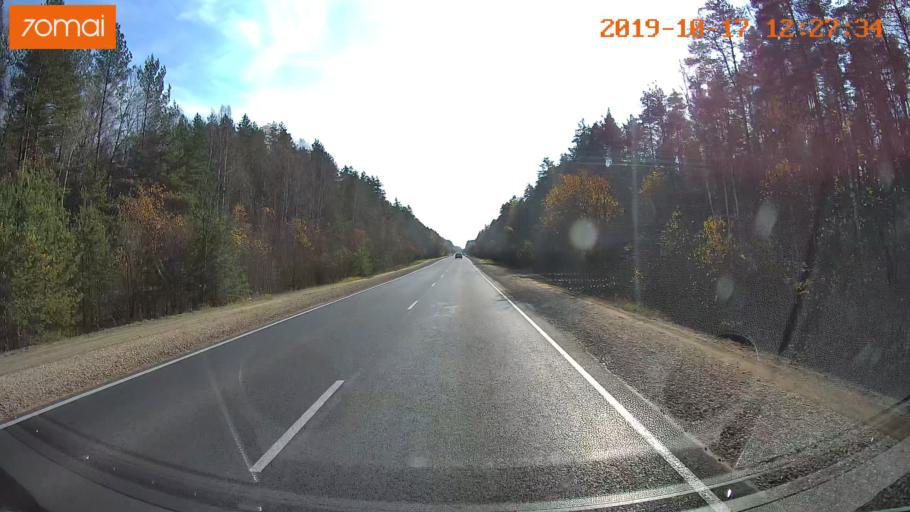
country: RU
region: Rjazan
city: Syntul
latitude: 55.0021
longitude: 41.2637
